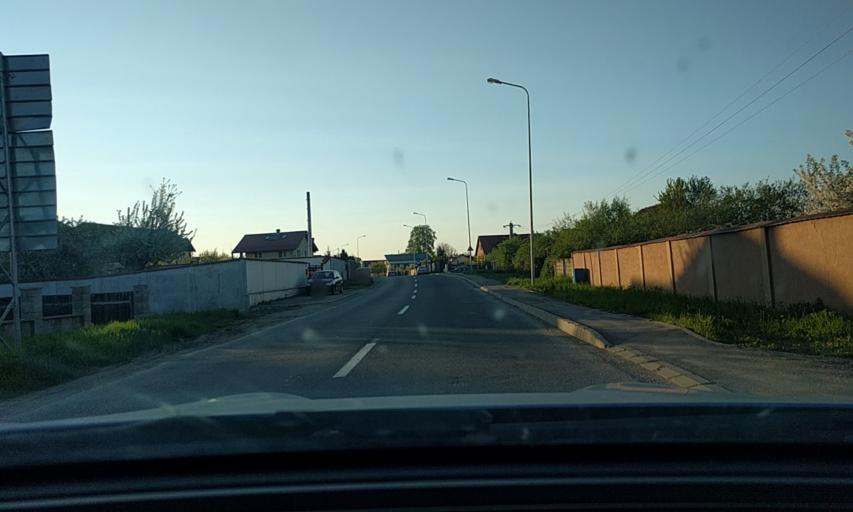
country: RO
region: Brasov
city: Brasov
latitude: 45.6897
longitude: 25.5670
